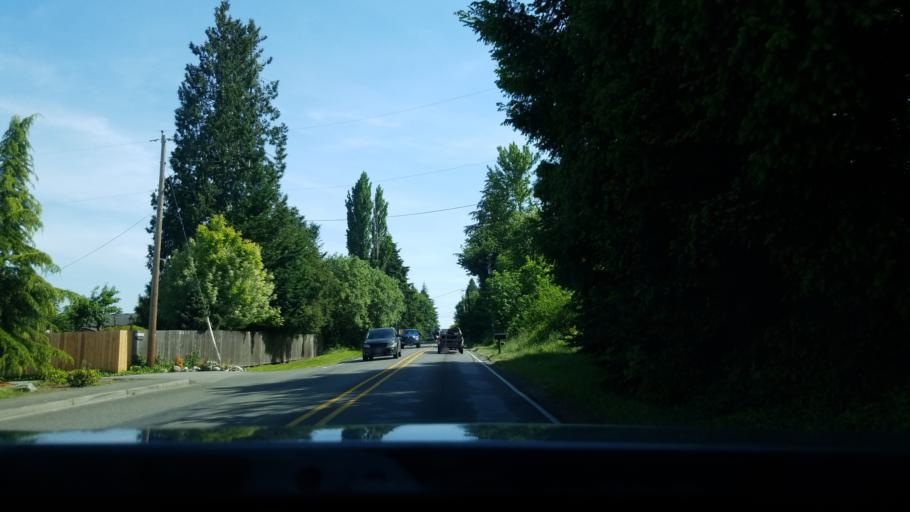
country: US
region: Washington
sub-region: Pierce County
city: Puyallup
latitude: 47.1666
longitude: -122.3042
